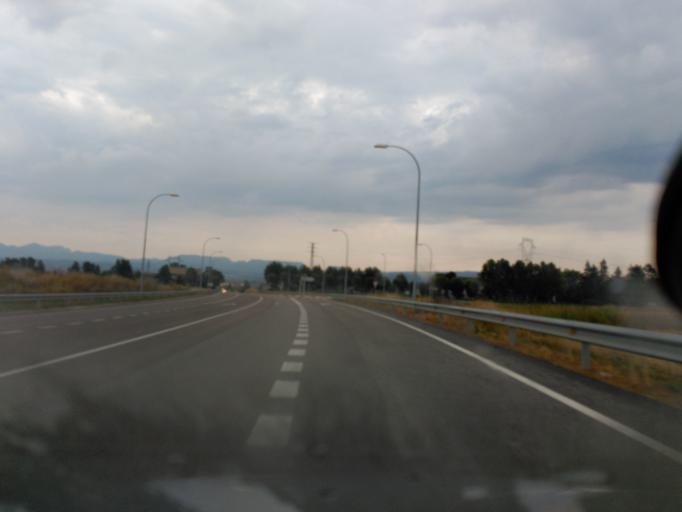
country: ES
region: Catalonia
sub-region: Provincia de Barcelona
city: Manlleu
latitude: 41.9613
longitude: 2.2911
